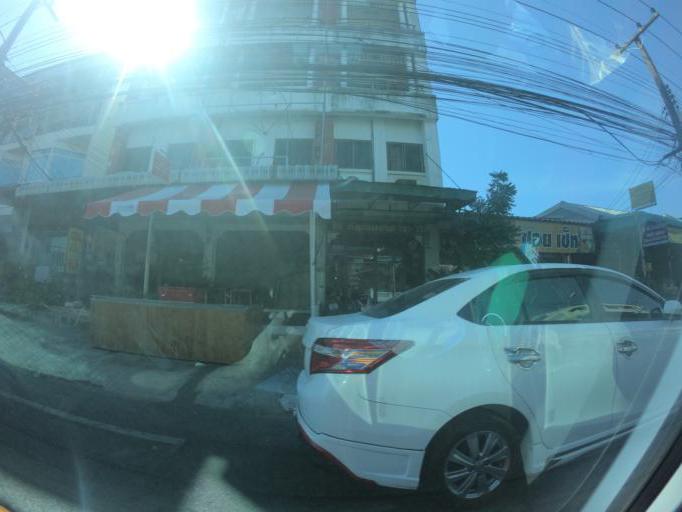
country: TH
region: Khon Kaen
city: Khon Kaen
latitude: 16.4162
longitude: 102.8342
